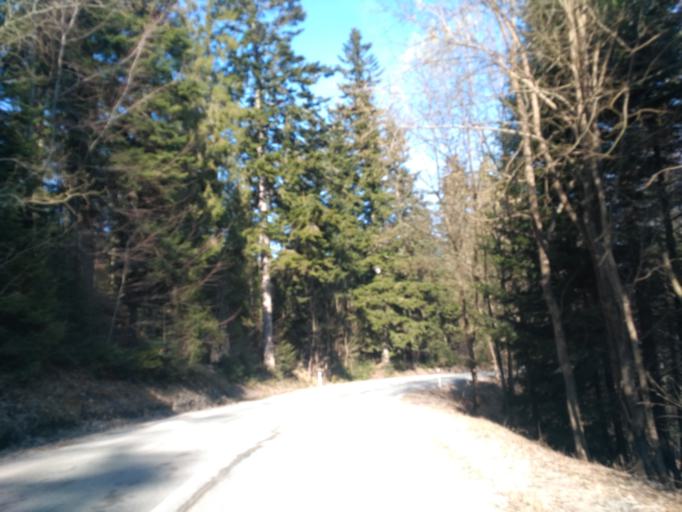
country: SK
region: Kosicky
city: Medzev
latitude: 48.7218
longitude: 20.7517
